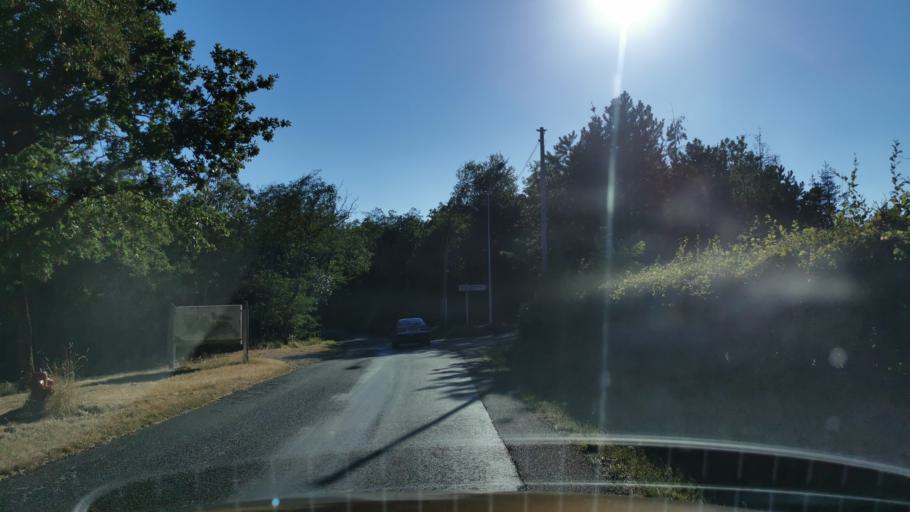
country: FR
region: Bourgogne
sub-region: Departement de Saone-et-Loire
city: Le Creusot
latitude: 46.8106
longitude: 4.4005
